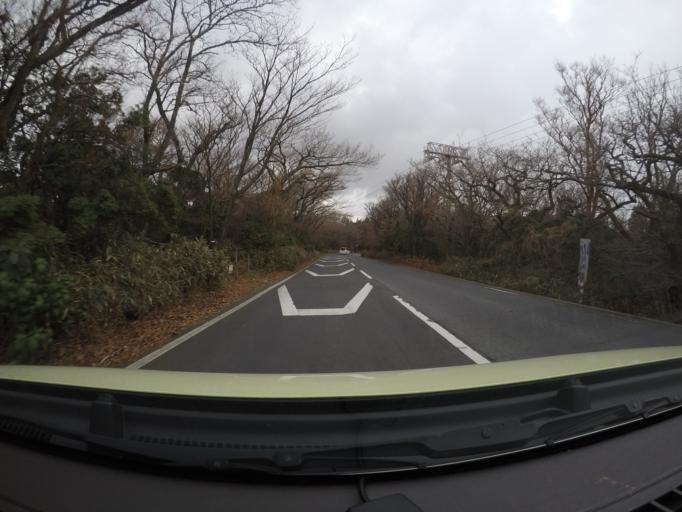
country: JP
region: Kanagawa
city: Hakone
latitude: 35.2440
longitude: 139.0173
